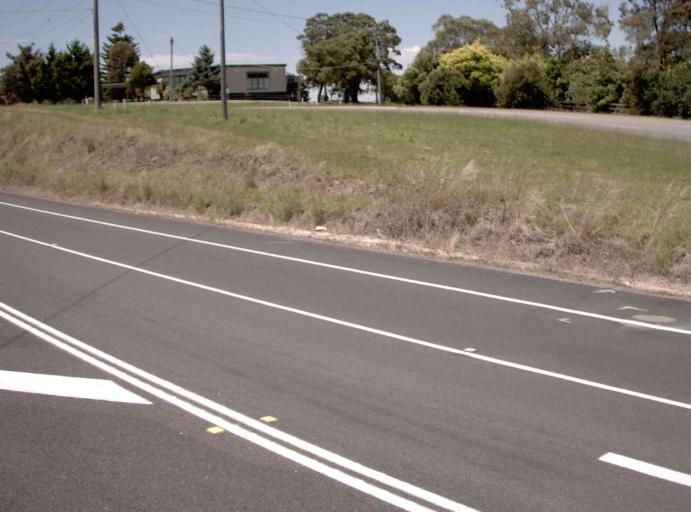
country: AU
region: Victoria
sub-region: East Gippsland
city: Lakes Entrance
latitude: -37.7064
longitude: 148.4688
